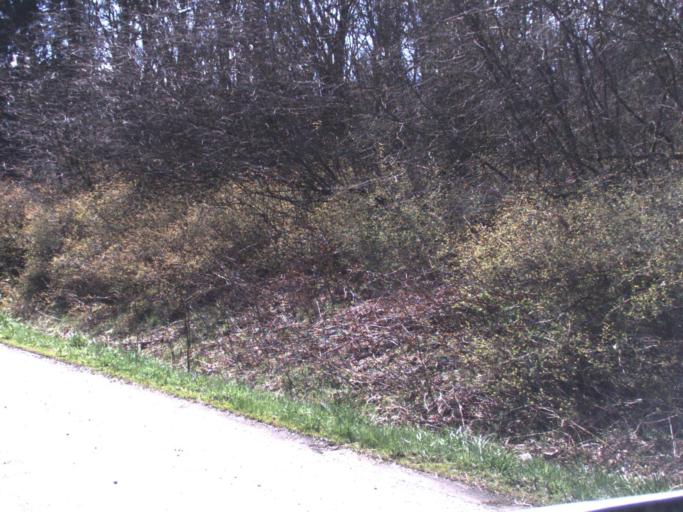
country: US
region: Washington
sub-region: King County
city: Enumclaw
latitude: 47.2486
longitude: -121.9899
